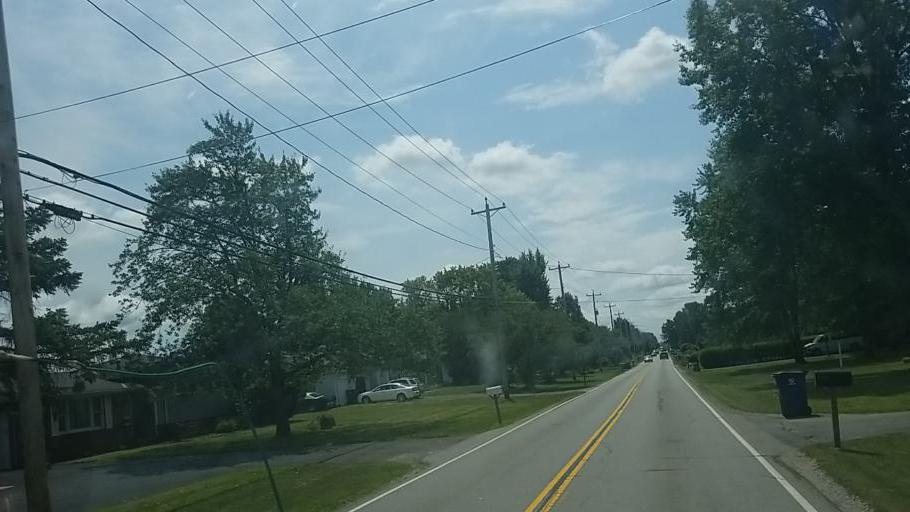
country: US
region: Ohio
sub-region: Franklin County
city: Reynoldsburg
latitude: 39.9933
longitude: -82.7674
